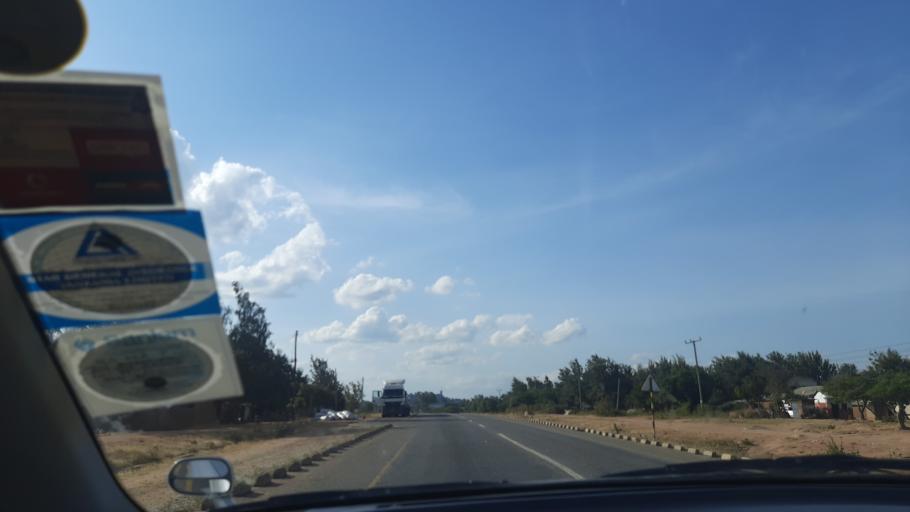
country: TZ
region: Singida
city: Puma
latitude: -5.0025
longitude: 34.7572
